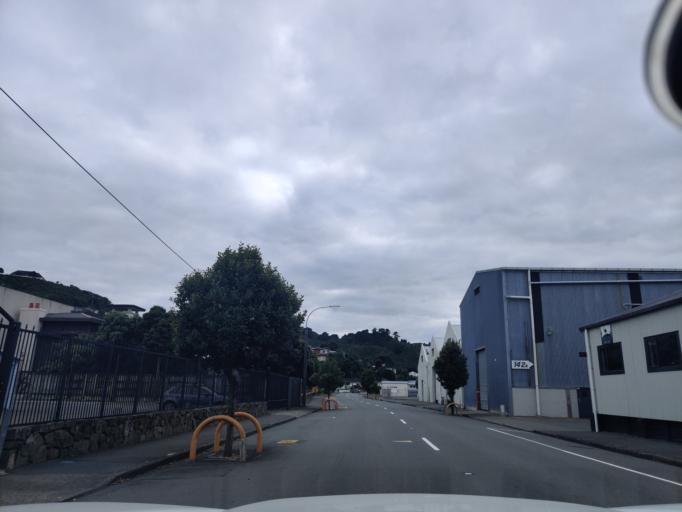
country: NZ
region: Wellington
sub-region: Wellington City
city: Wellington
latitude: -41.3088
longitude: 174.8216
